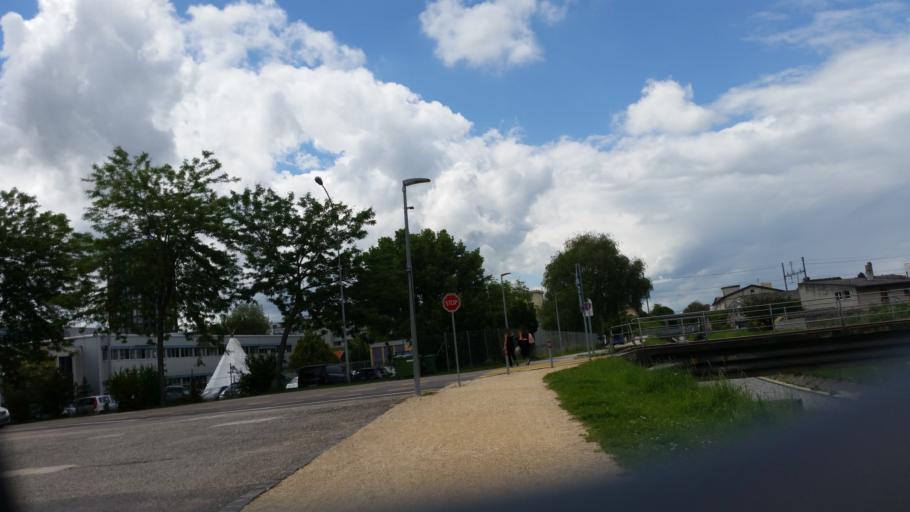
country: CH
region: Vaud
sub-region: Jura-Nord vaudois District
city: Yverdon-les-Bains
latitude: 46.7810
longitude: 6.6518
